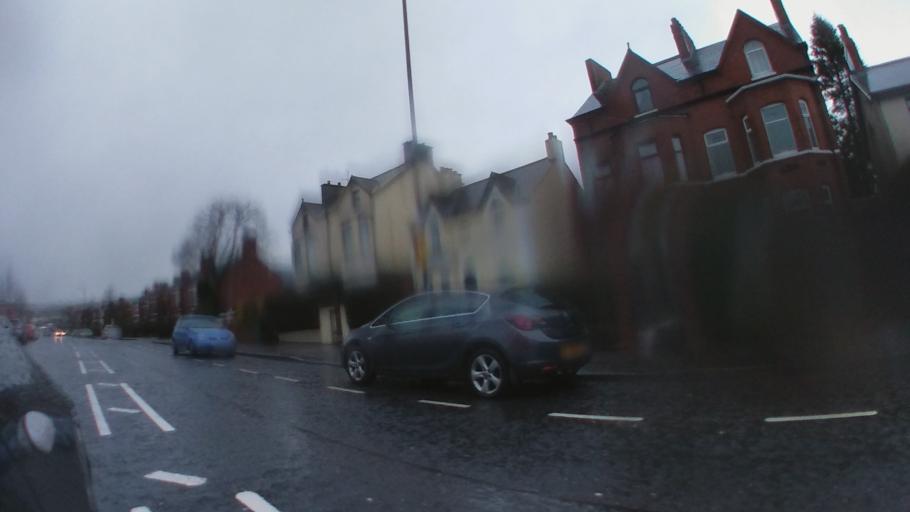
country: GB
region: Northern Ireland
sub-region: City of Belfast
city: Belfast
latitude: 54.6221
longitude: -5.9568
